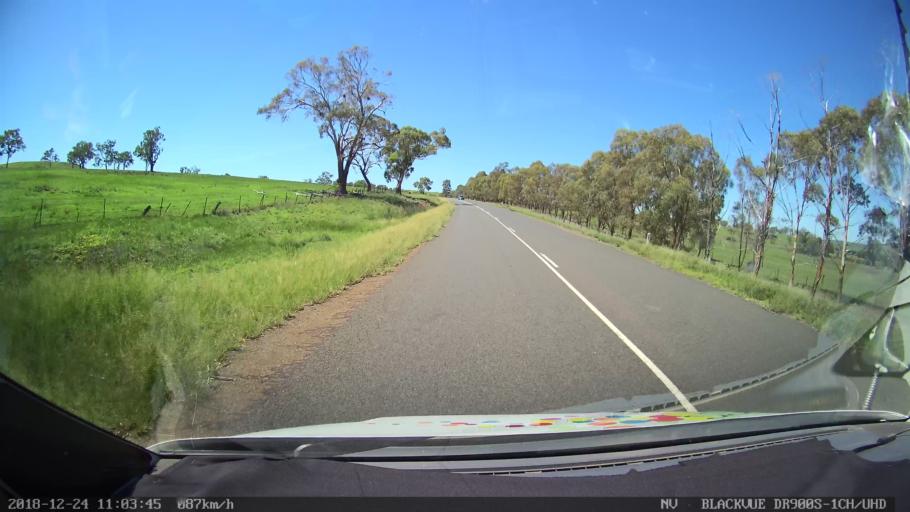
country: AU
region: New South Wales
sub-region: Upper Hunter Shire
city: Merriwa
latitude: -32.1007
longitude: 150.3689
